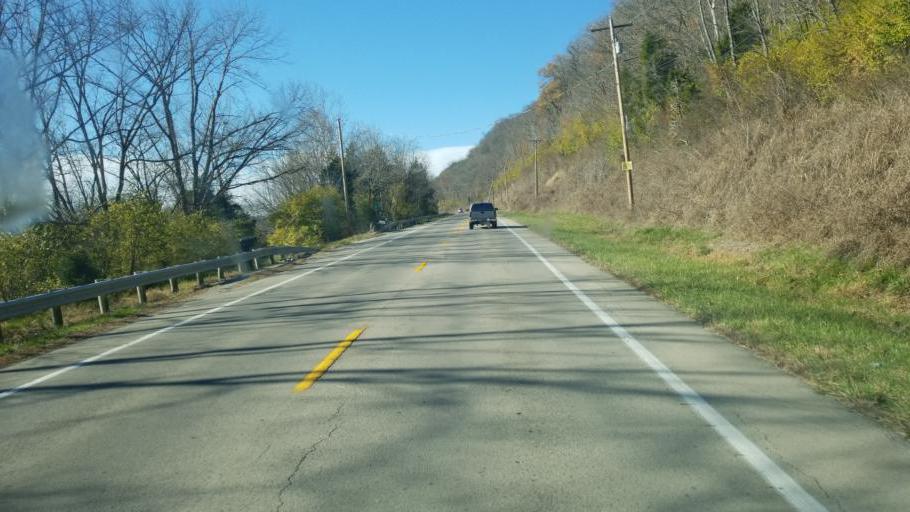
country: US
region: Kentucky
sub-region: Mason County
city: Maysville
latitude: 38.6480
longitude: -83.7200
